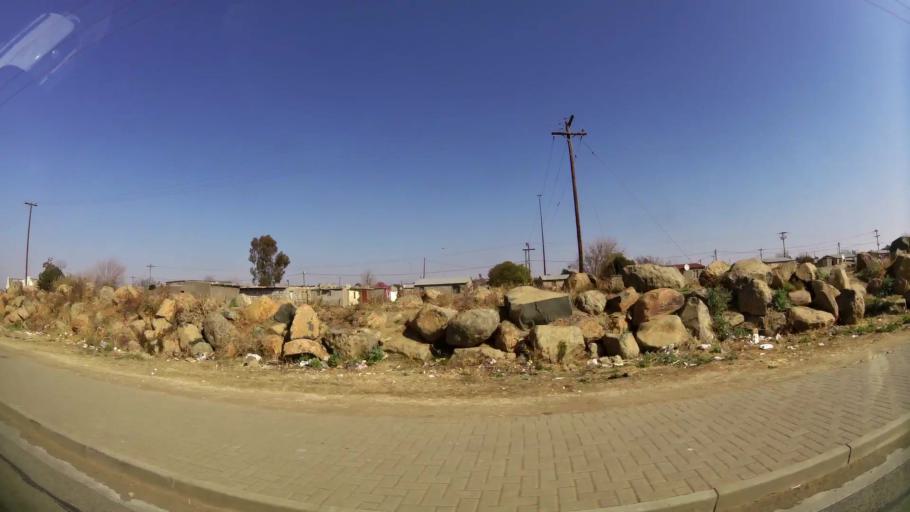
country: ZA
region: Orange Free State
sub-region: Mangaung Metropolitan Municipality
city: Bloemfontein
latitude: -29.1592
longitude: 26.2554
